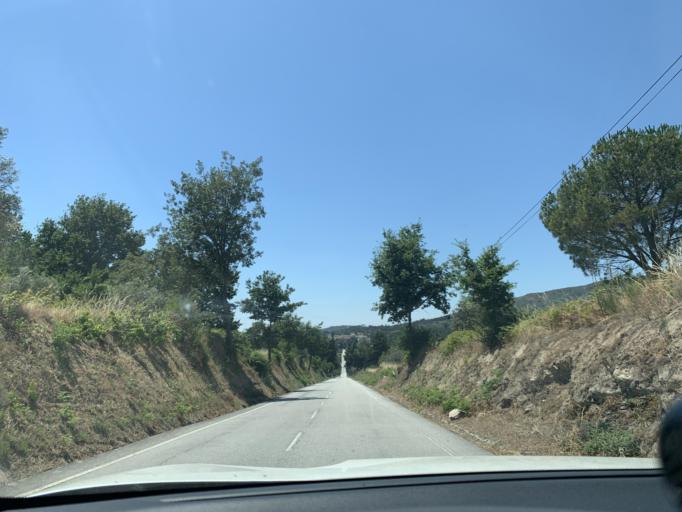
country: PT
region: Guarda
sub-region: Fornos de Algodres
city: Fornos de Algodres
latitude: 40.5816
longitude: -7.6236
